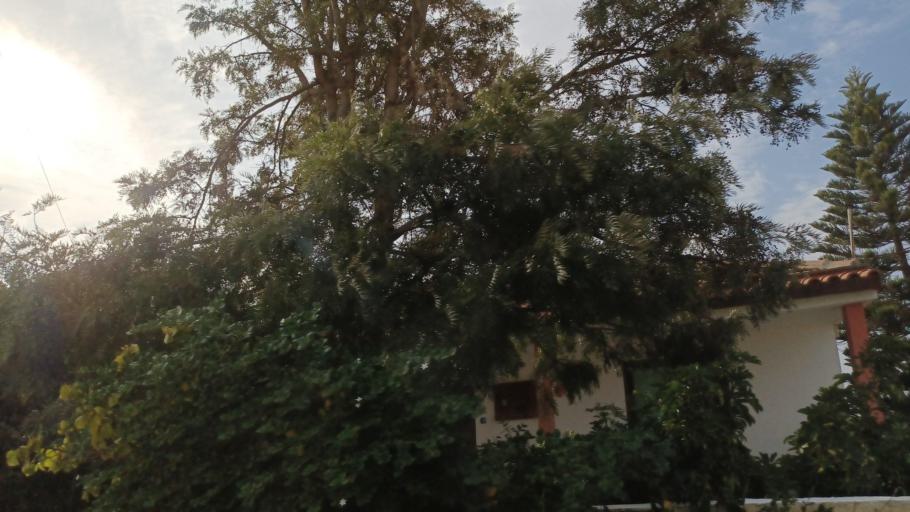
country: CY
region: Lefkosia
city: Peristerona
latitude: 35.0986
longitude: 33.0940
